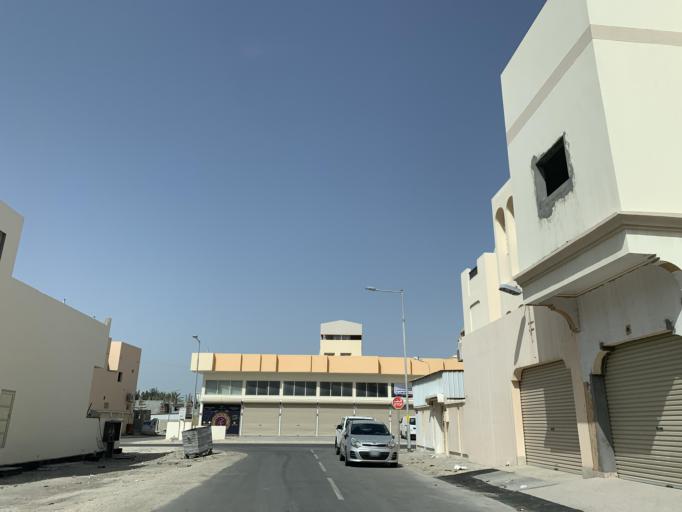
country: BH
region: Northern
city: Sitrah
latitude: 26.1441
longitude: 50.6045
